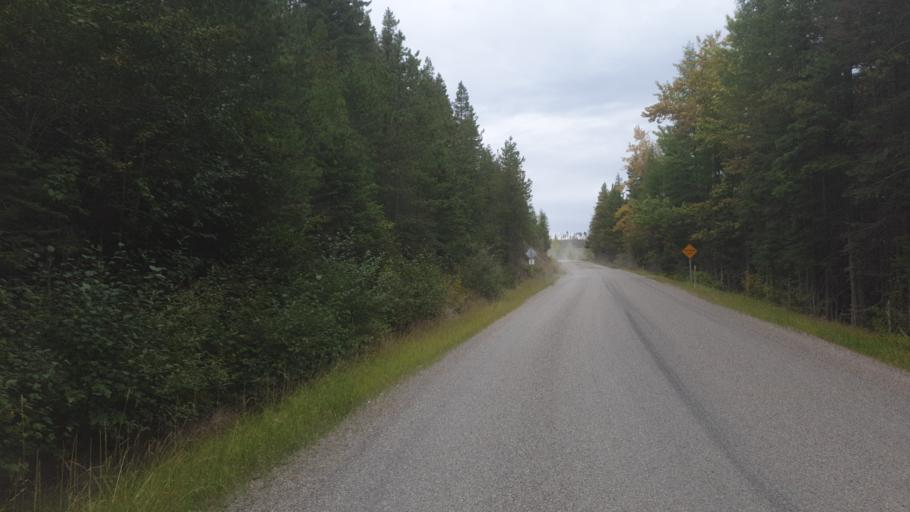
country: US
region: Montana
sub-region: Flathead County
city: Lakeside
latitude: 47.9867
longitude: -114.3148
